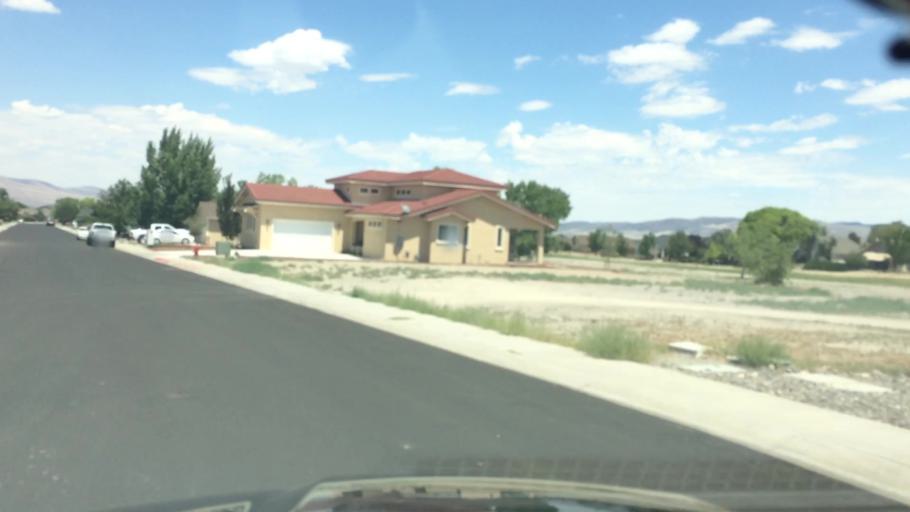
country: US
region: Nevada
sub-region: Lyon County
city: Fernley
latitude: 39.5839
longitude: -119.1411
